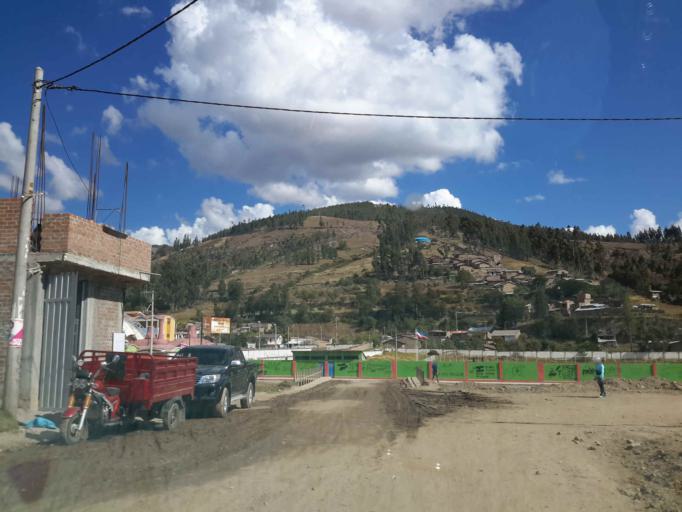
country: PE
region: Apurimac
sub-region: Provincia de Andahuaylas
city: Talavera
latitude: -13.6567
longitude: -73.4319
